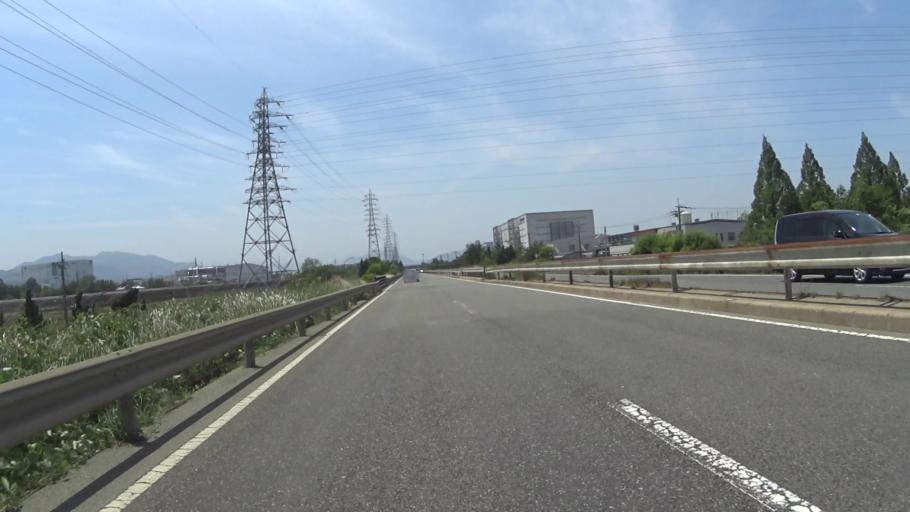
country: JP
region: Kyoto
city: Fukuchiyama
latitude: 35.2843
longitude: 135.1720
